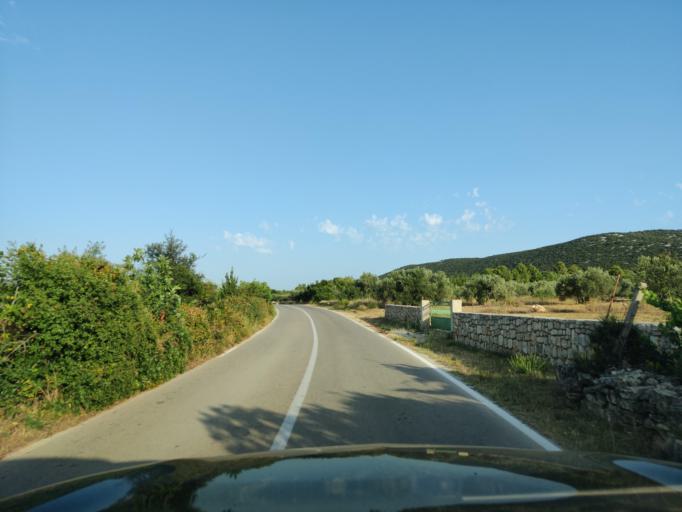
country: HR
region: Sibensko-Kniniska
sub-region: Grad Sibenik
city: Pirovac
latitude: 43.7915
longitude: 15.6932
